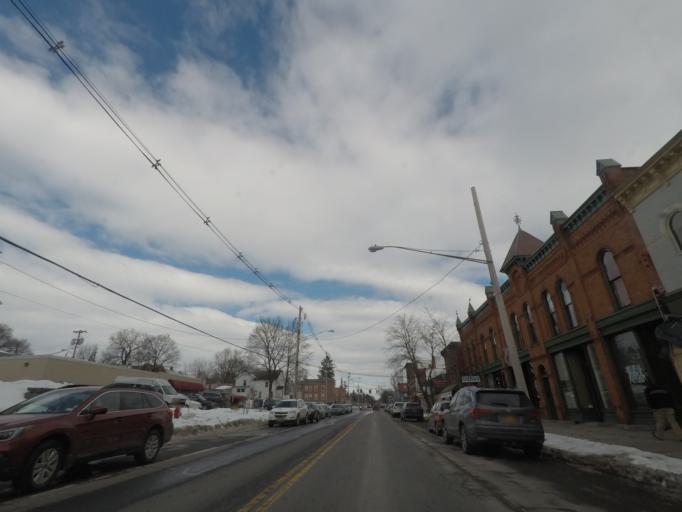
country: US
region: New York
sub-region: Saratoga County
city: Schuylerville
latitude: 43.0988
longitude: -73.5817
